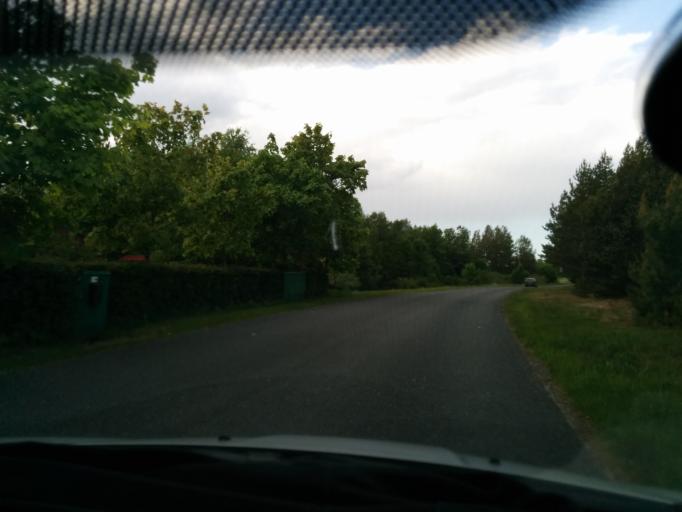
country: EE
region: Harju
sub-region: Loksa linn
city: Loksa
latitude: 59.6500
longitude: 25.6968
